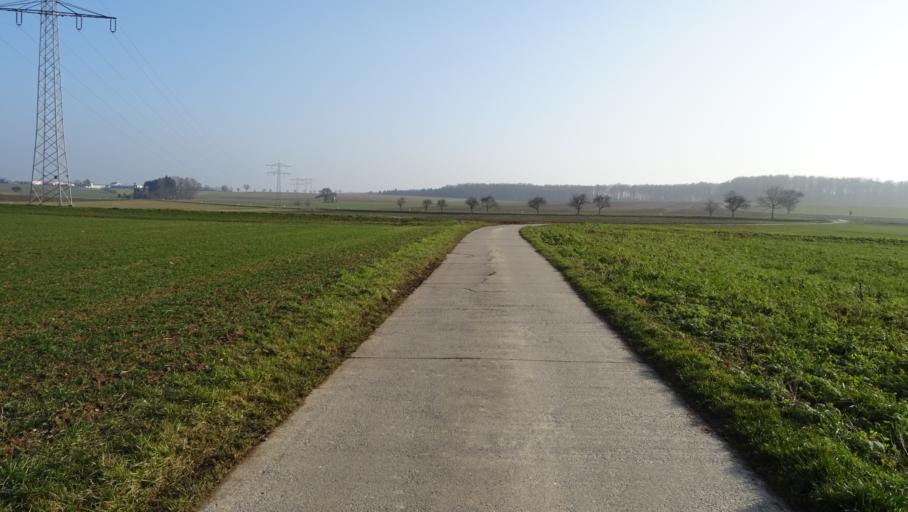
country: DE
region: Baden-Wuerttemberg
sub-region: Karlsruhe Region
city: Neckargerach
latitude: 49.3981
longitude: 9.1058
